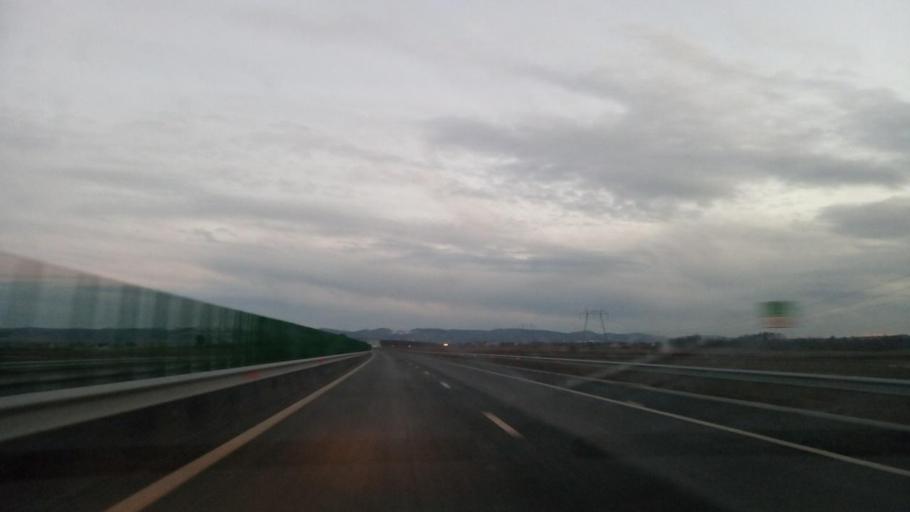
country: RO
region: Bacau
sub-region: Comuna Saucesti
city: Saucesti
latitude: 46.6312
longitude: 26.9387
